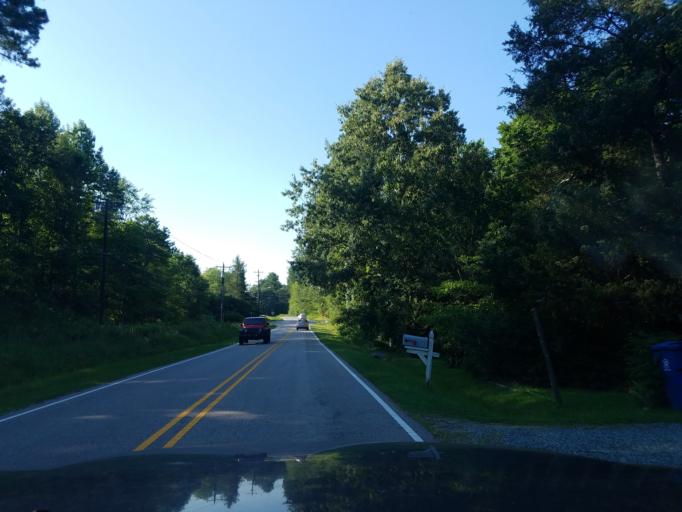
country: US
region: North Carolina
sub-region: Wake County
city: Green Level
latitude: 35.8813
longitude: -78.9153
